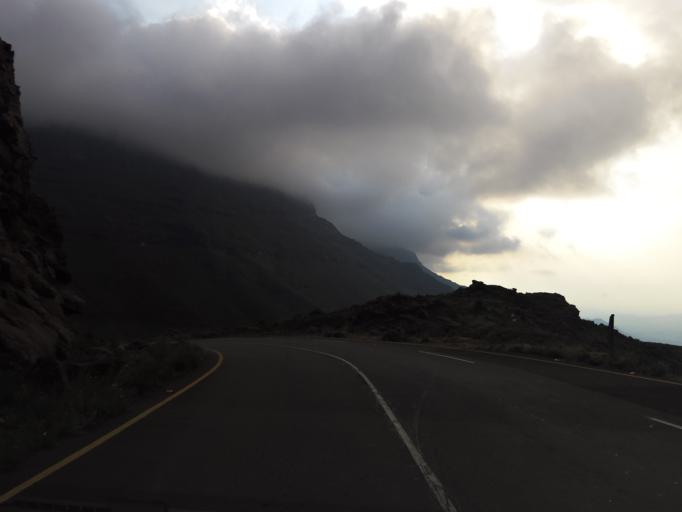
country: LS
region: Butha-Buthe
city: Butha-Buthe
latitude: -29.0687
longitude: 28.3804
